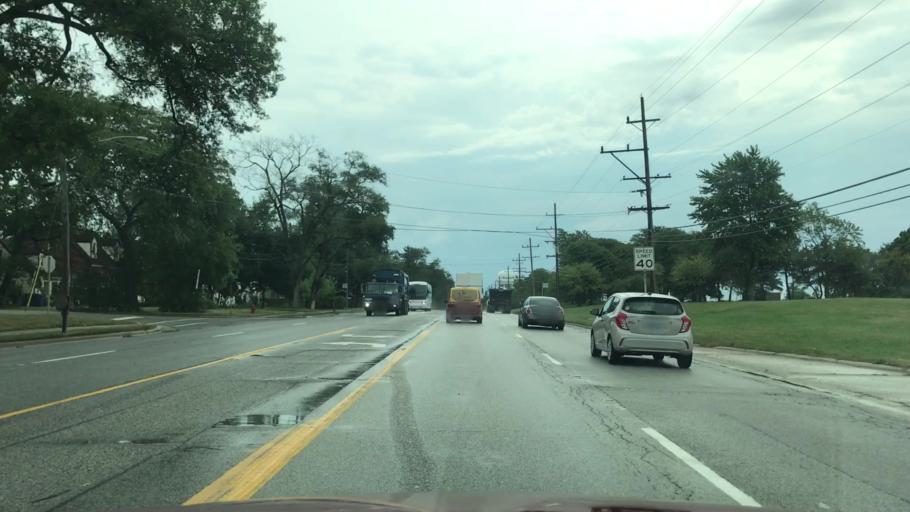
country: US
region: Illinois
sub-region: Cook County
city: Elk Grove Village
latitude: 42.0227
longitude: -87.9356
